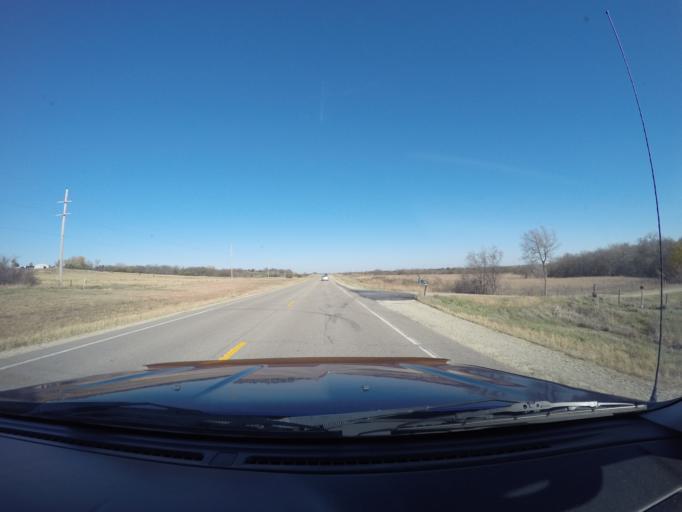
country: US
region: Kansas
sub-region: Riley County
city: Ogden
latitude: 39.3562
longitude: -96.7565
